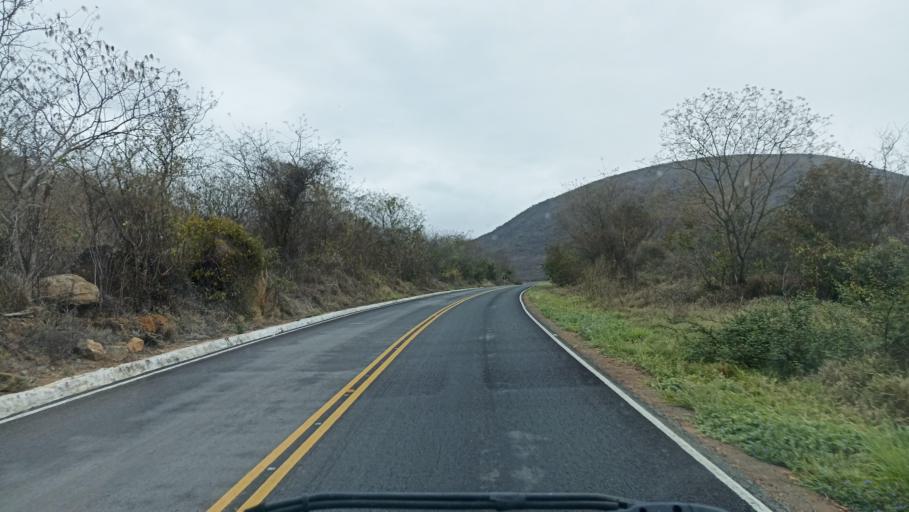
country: BR
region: Bahia
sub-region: Andarai
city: Vera Cruz
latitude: -13.0486
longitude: -40.7805
